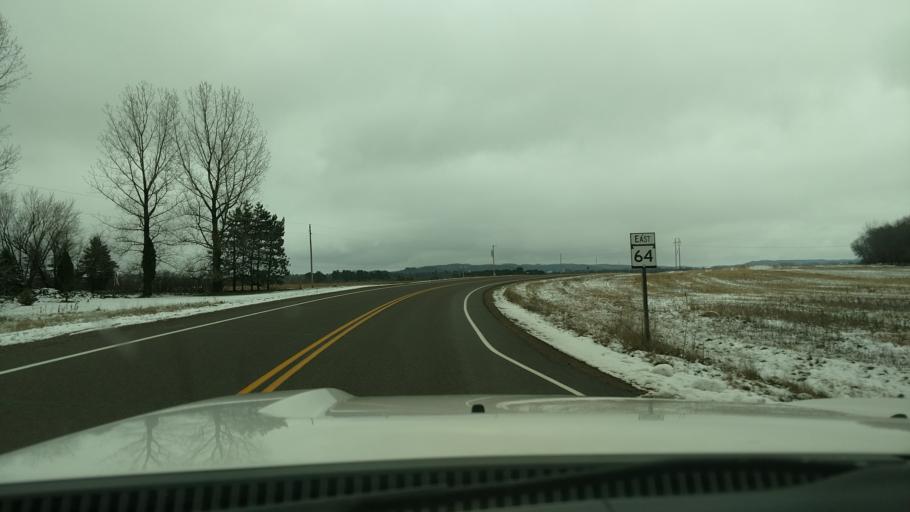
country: US
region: Wisconsin
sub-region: Dunn County
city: Colfax
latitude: 45.1430
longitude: -91.7281
